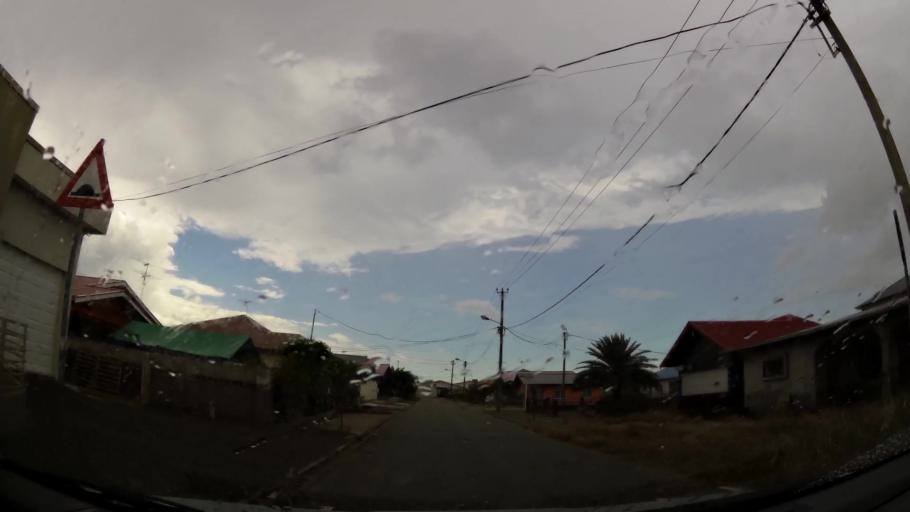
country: SR
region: Commewijne
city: Nieuw Amsterdam
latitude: 5.8539
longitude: -55.1169
